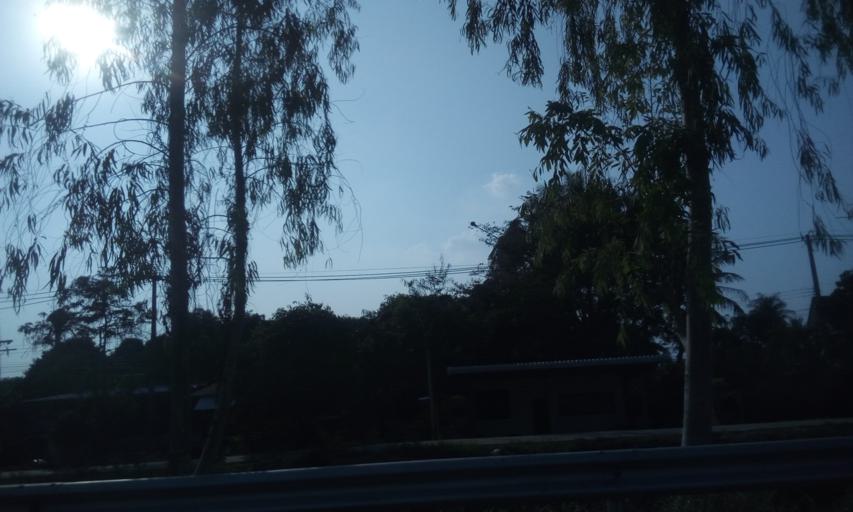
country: TH
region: Sing Buri
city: Sing Buri
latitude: 14.8645
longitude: 100.4049
